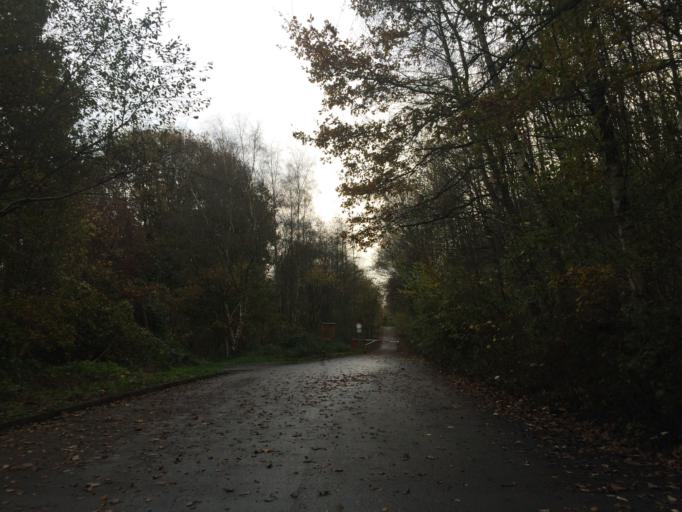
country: DE
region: North Rhine-Westphalia
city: Marl
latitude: 51.6818
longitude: 7.0713
